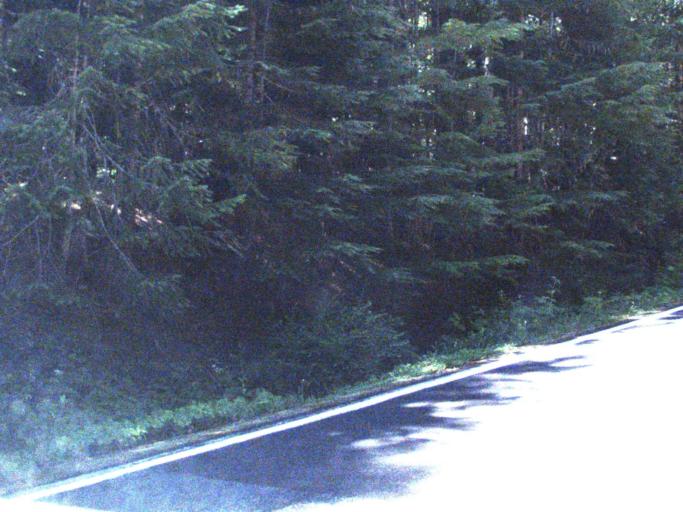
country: US
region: Washington
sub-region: King County
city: Enumclaw
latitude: 46.8079
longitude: -121.5552
